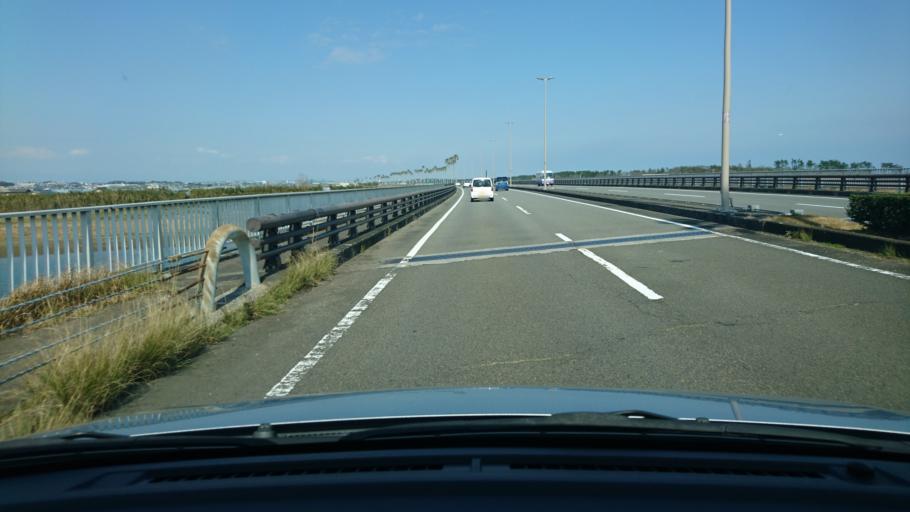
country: JP
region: Miyazaki
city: Miyazaki-shi
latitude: 31.8350
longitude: 131.4446
